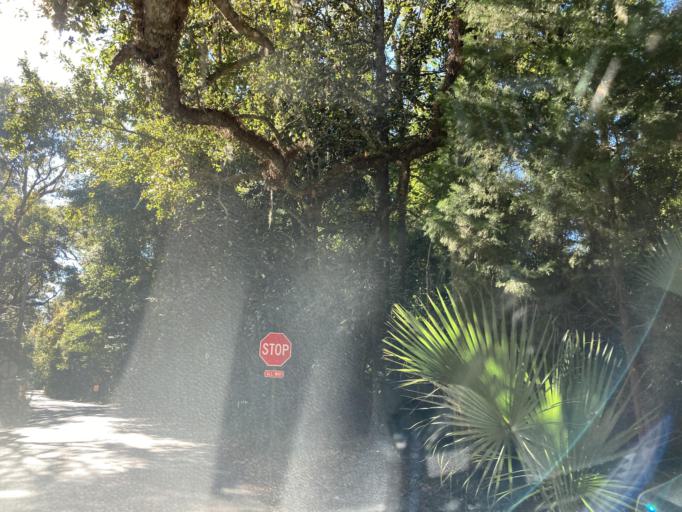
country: US
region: Mississippi
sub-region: Jackson County
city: Ocean Springs
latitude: 30.4155
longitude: -88.8415
